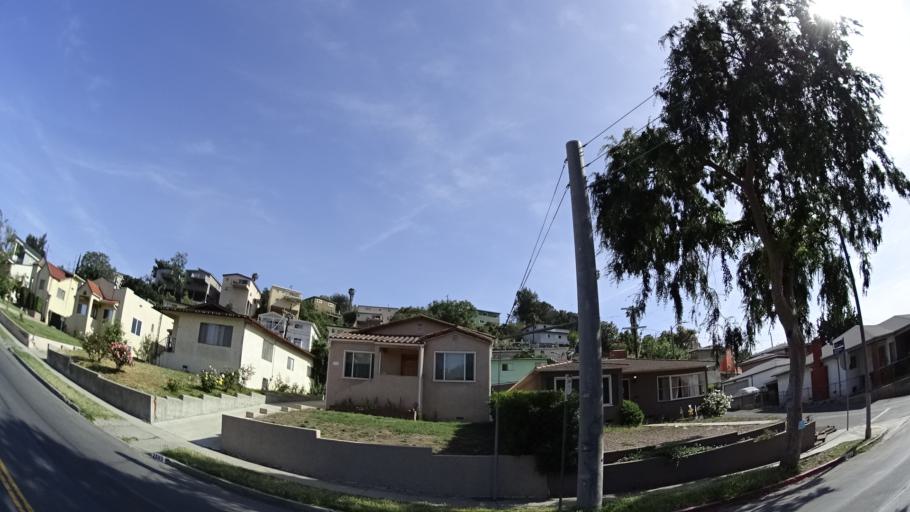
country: US
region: California
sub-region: Los Angeles County
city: Belvedere
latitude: 34.0766
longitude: -118.1763
